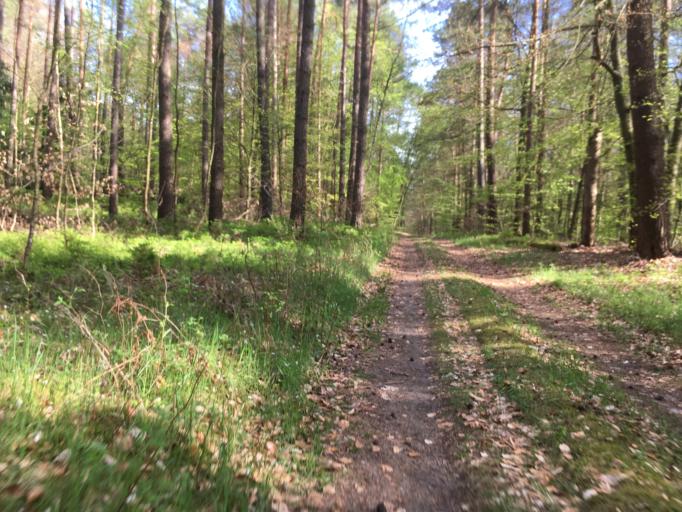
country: DE
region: Brandenburg
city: Bernau bei Berlin
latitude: 52.7203
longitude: 13.5619
